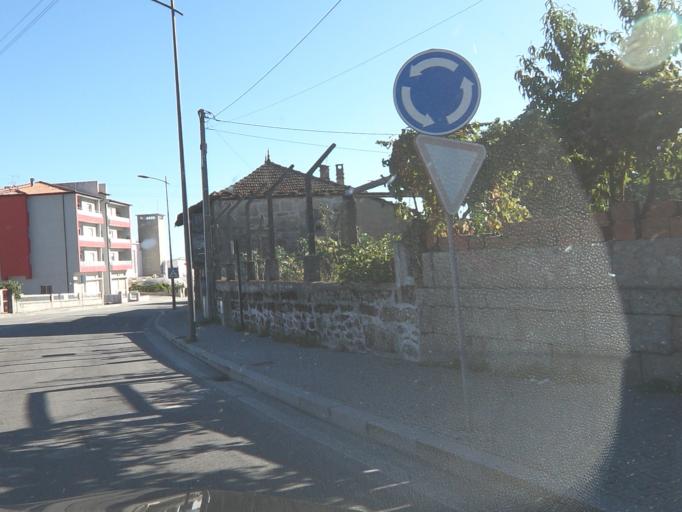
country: PT
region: Vila Real
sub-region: Valpacos
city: Valpacos
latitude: 41.6023
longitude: -7.3084
